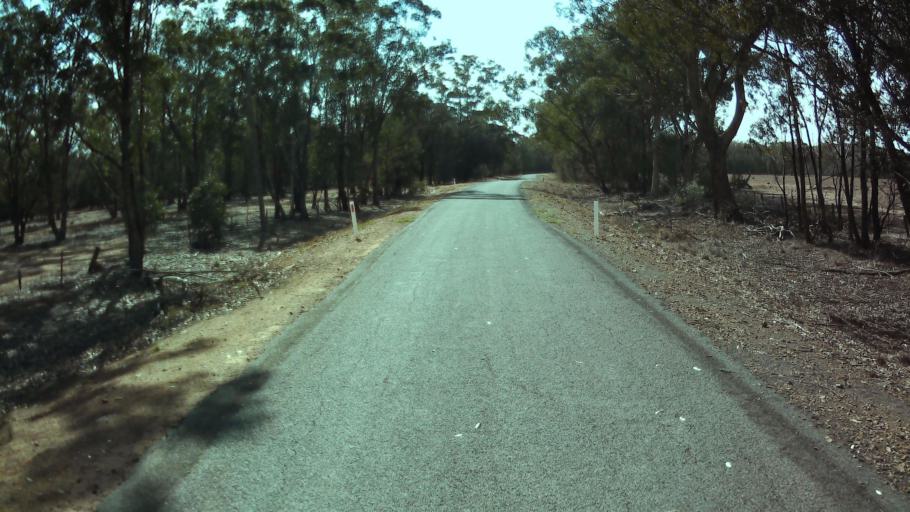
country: AU
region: New South Wales
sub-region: Weddin
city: Grenfell
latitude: -33.7105
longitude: 148.0181
